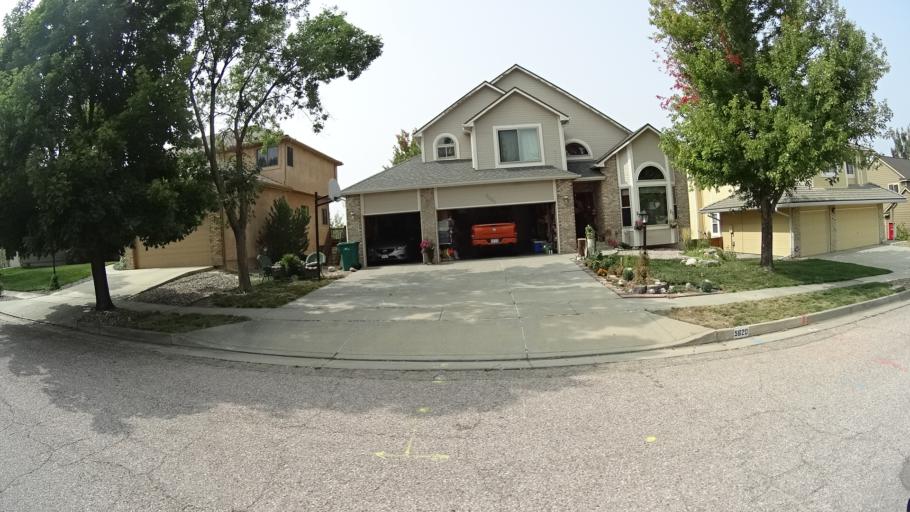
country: US
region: Colorado
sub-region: El Paso County
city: Cimarron Hills
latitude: 38.9183
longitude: -104.7422
